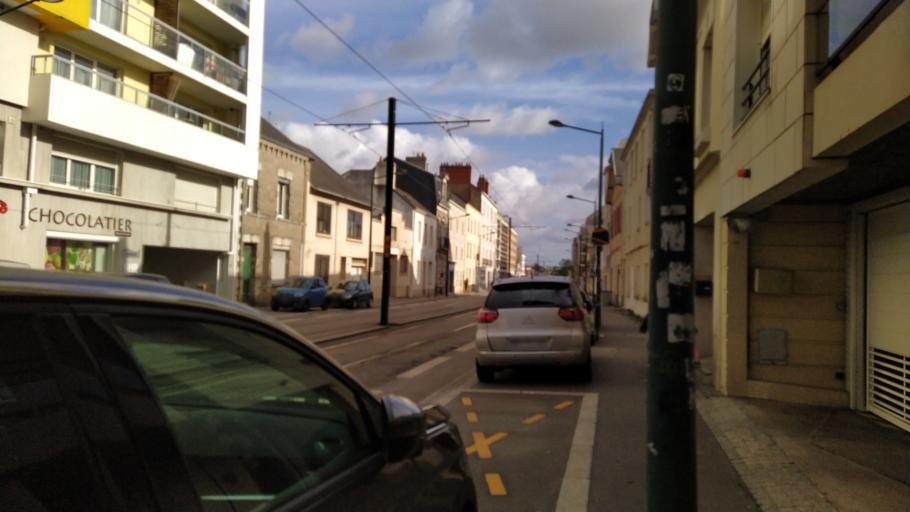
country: FR
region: Pays de la Loire
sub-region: Departement de la Loire-Atlantique
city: Nantes
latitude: 47.2284
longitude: -1.5712
